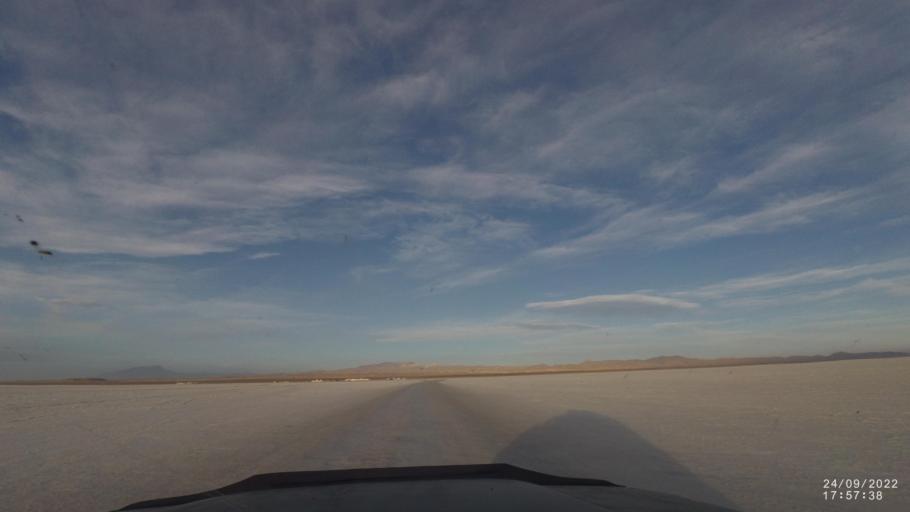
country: BO
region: Potosi
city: Colchani
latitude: -20.3194
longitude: -66.9889
